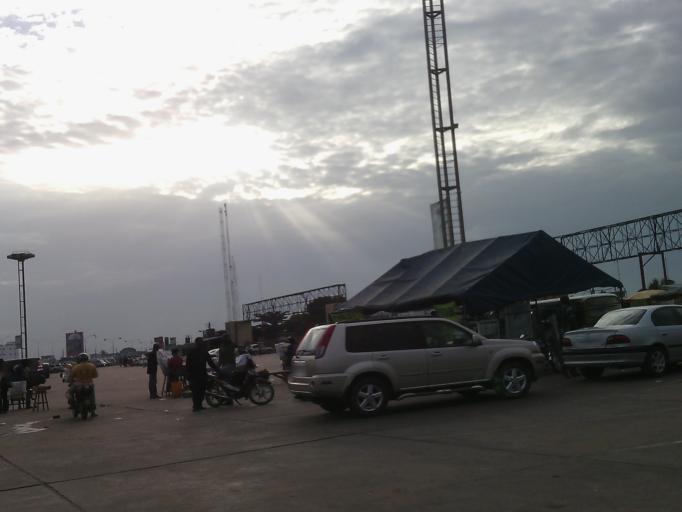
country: BJ
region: Littoral
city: Cotonou
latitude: 6.3844
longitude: 2.3785
